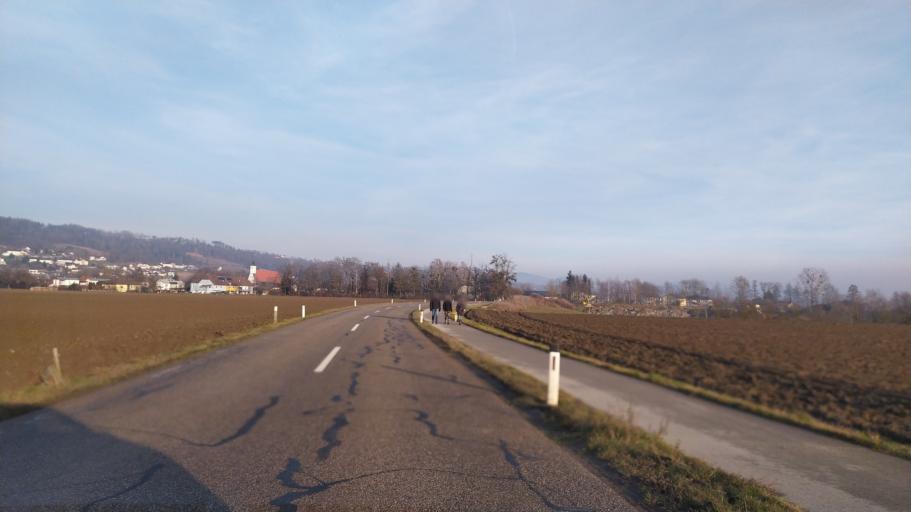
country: AT
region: Upper Austria
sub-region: Politischer Bezirk Urfahr-Umgebung
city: Feldkirchen an der Donau
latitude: 48.3471
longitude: 14.0655
